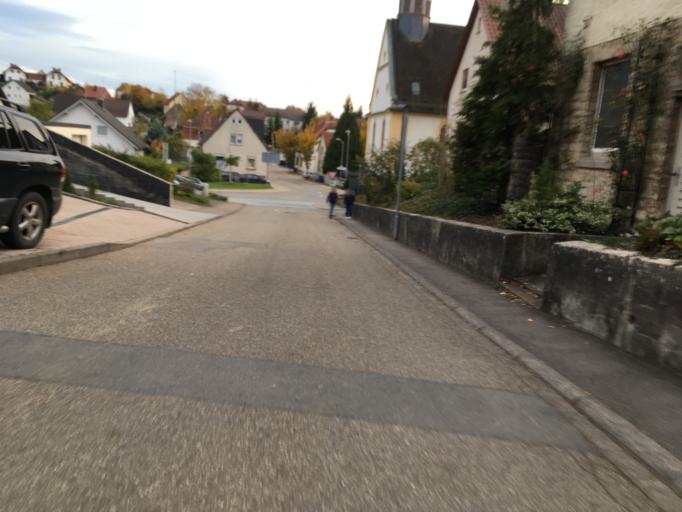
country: DE
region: Baden-Wuerttemberg
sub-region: Regierungsbezirk Stuttgart
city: Kirchardt
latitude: 49.2273
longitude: 8.9945
